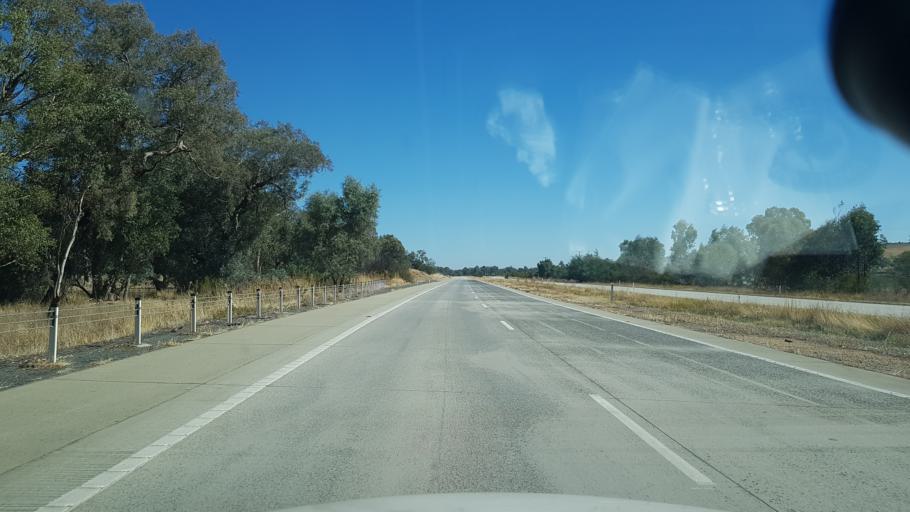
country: AU
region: New South Wales
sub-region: Greater Hume Shire
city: Holbrook
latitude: -35.9052
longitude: 147.1619
